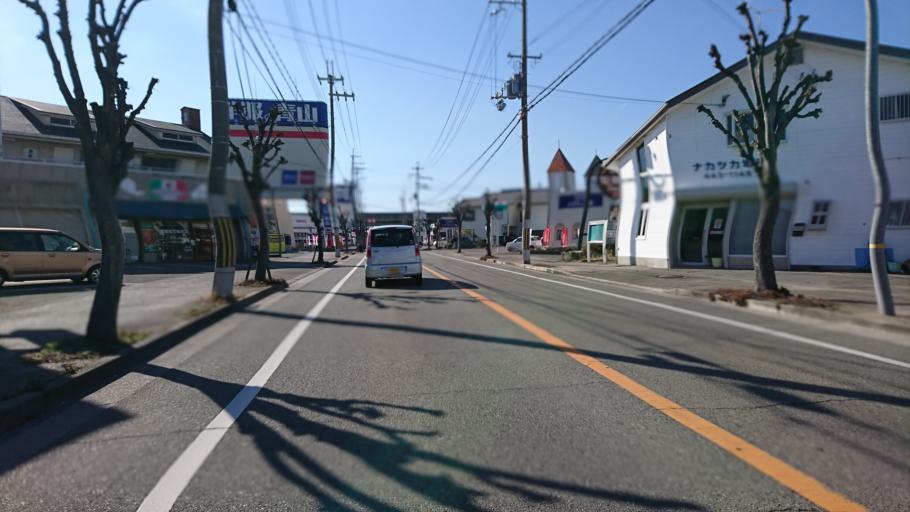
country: JP
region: Hyogo
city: Kakogawacho-honmachi
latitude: 34.7683
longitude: 134.8005
